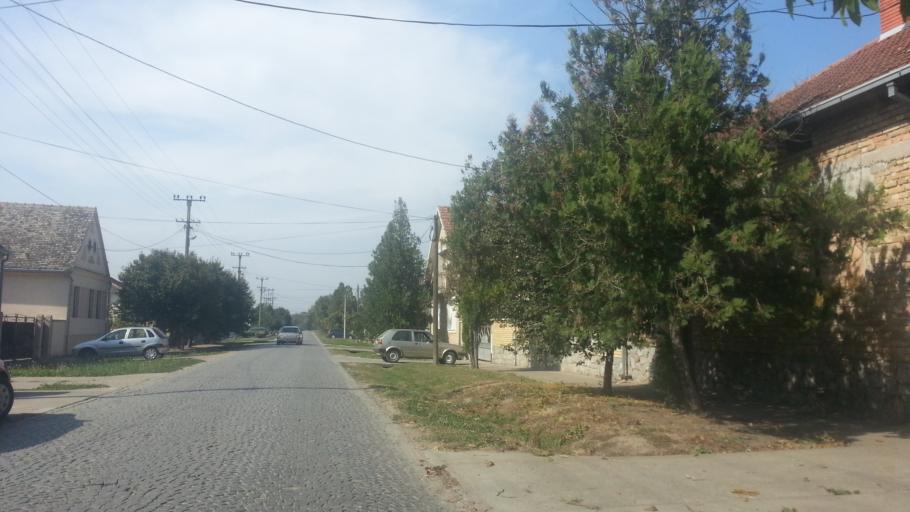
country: RS
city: Stari Banovci
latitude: 44.9950
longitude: 20.2832
